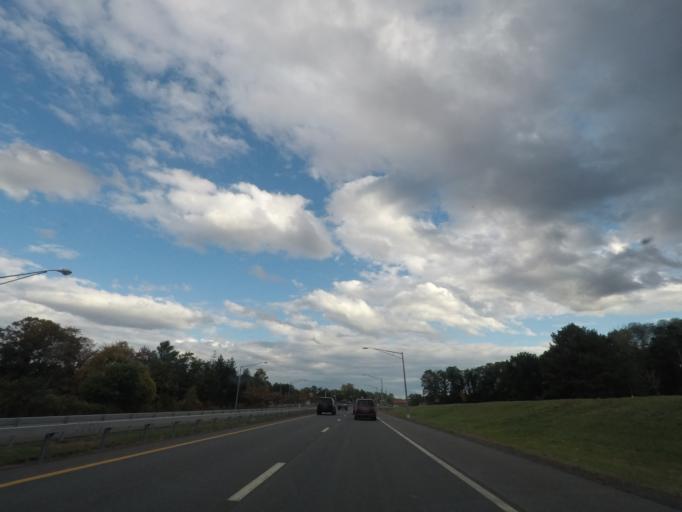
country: US
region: New York
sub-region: Albany County
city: Westmere
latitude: 42.7030
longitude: -73.8550
